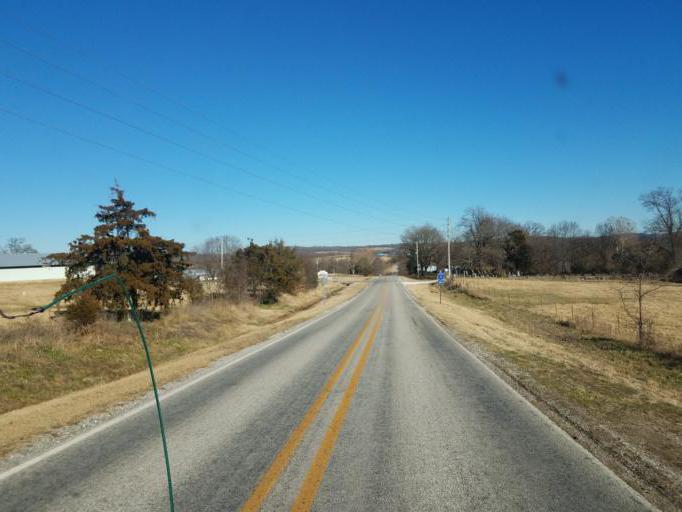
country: US
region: Arkansas
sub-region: Washington County
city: Elkins
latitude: 36.0331
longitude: -93.9739
